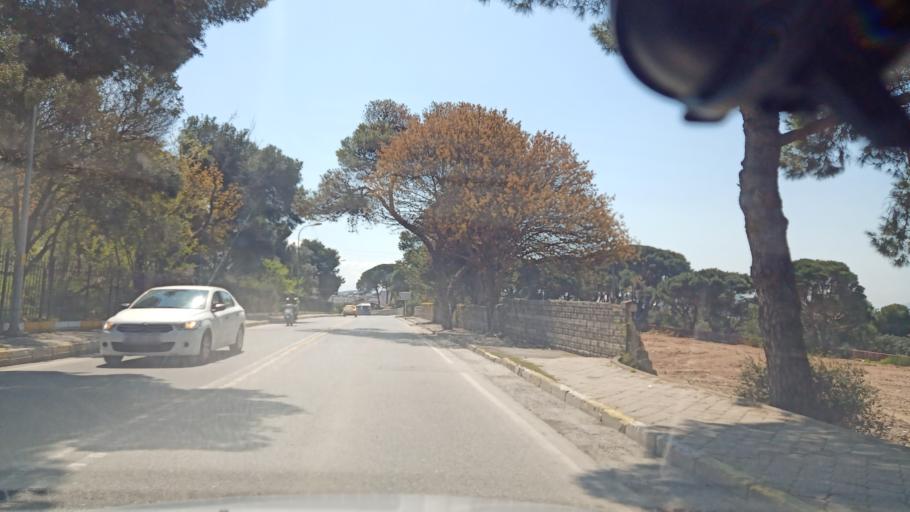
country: TR
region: Istanbul
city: Maltepe
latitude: 40.9499
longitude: 29.1423
